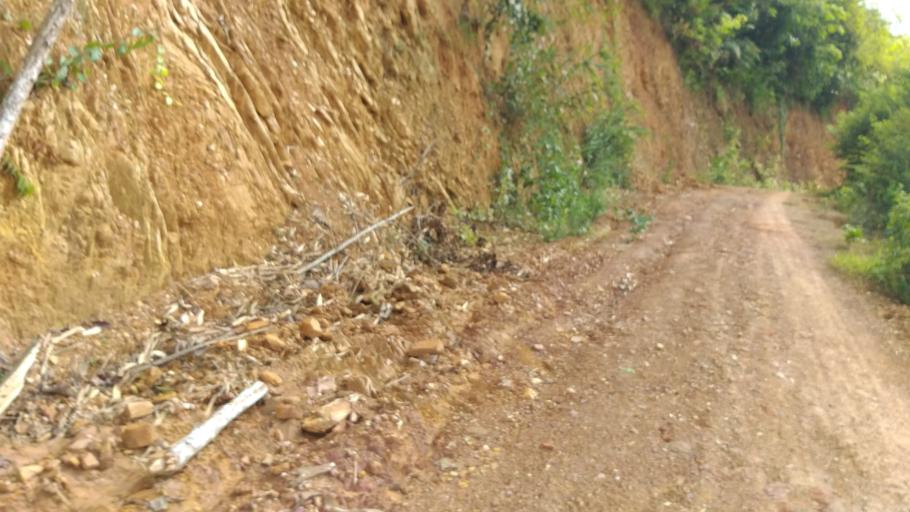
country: LA
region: Phongsali
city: Khoa
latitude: 21.2740
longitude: 102.5226
